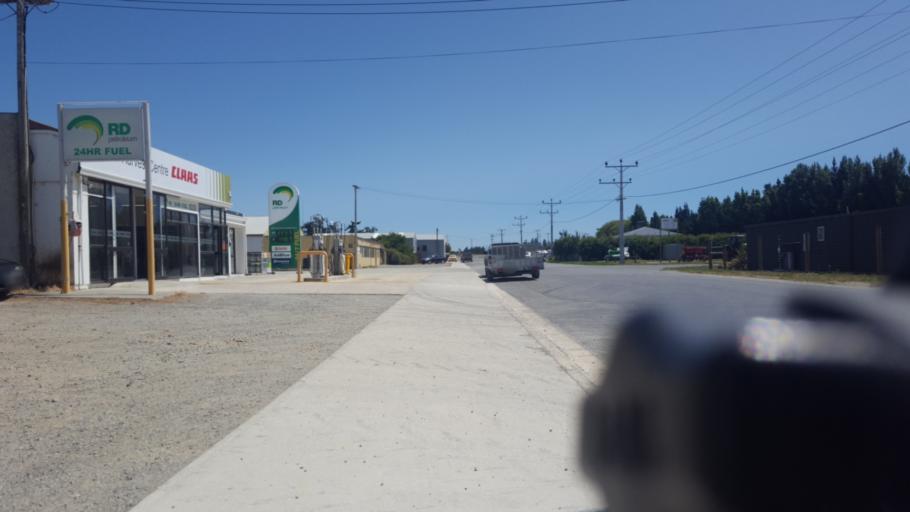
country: NZ
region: Otago
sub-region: Dunedin City
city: Dunedin
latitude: -45.1295
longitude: 170.0971
